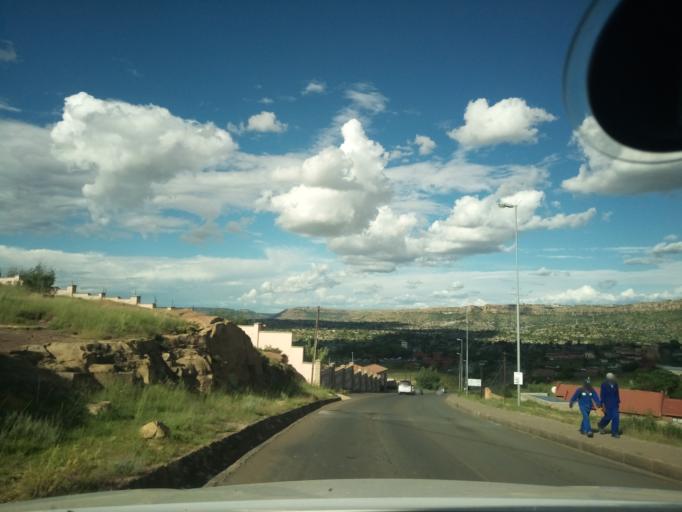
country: LS
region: Maseru
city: Maseru
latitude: -29.3282
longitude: 27.4957
